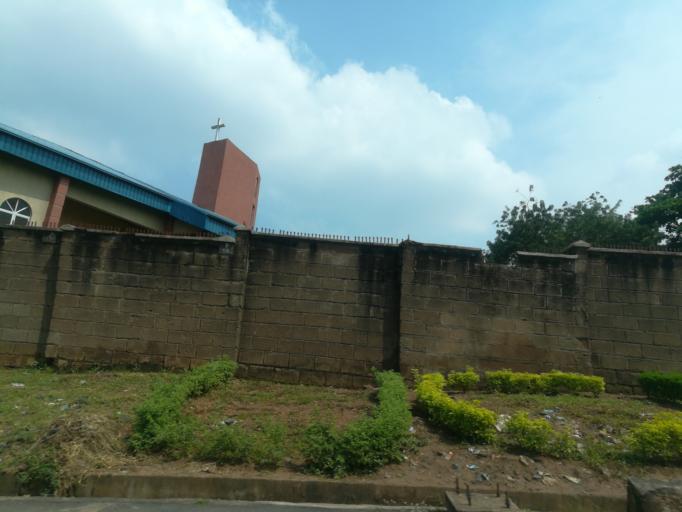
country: NG
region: Oyo
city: Ibadan
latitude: 7.4014
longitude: 3.8976
